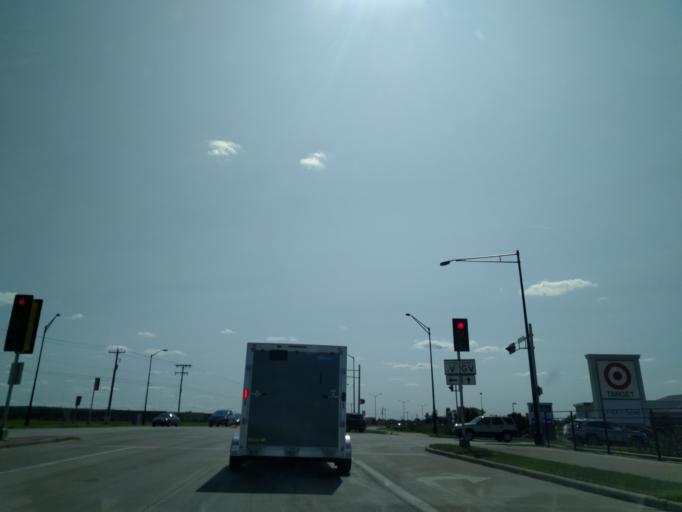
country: US
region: Wisconsin
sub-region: Brown County
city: Allouez
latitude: 44.4639
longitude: -87.9831
